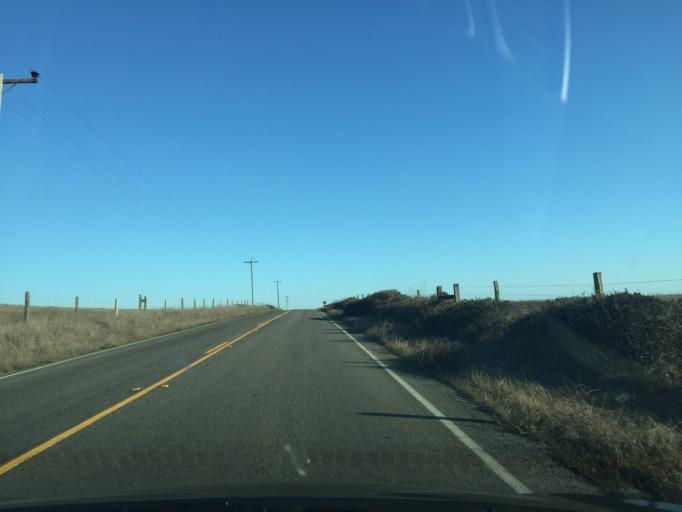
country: US
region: California
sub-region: San Luis Obispo County
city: Cambria
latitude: 35.6725
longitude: -121.2809
